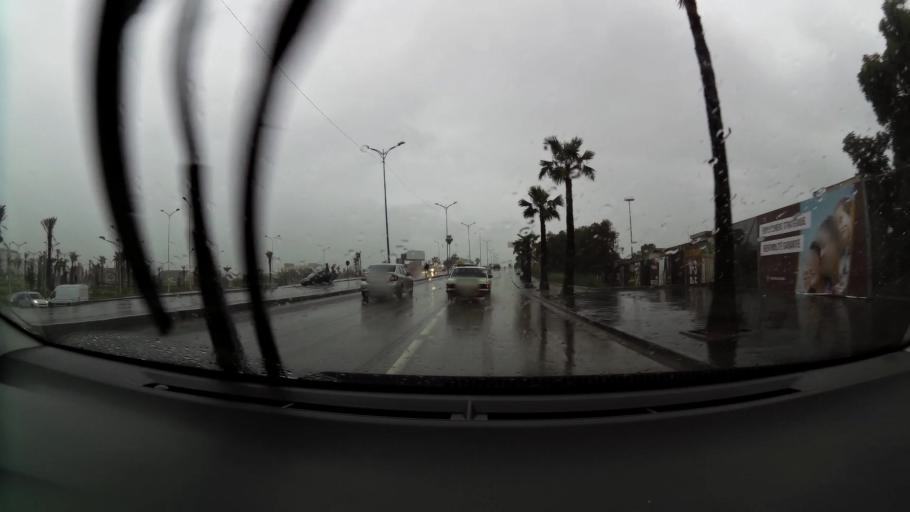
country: MA
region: Grand Casablanca
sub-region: Mediouna
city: Tit Mellil
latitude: 33.6015
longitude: -7.5103
